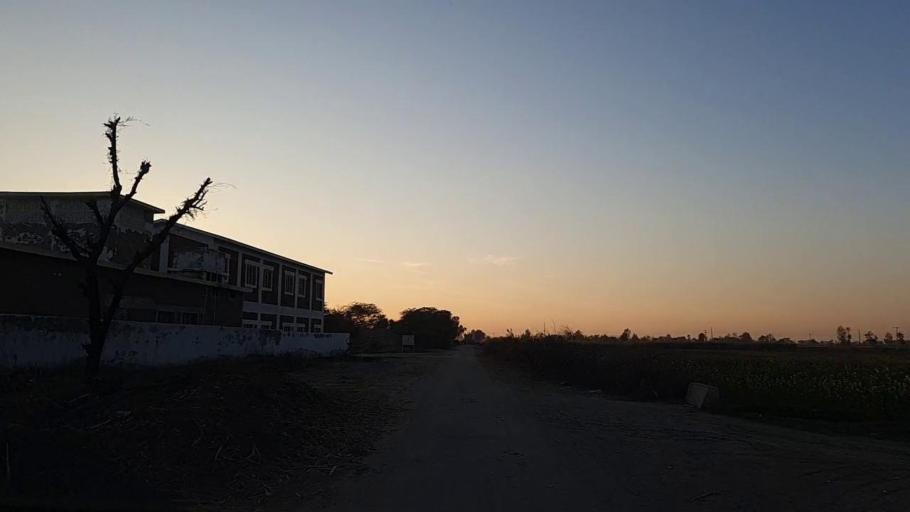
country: PK
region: Sindh
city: Bandhi
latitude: 26.6201
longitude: 68.3626
